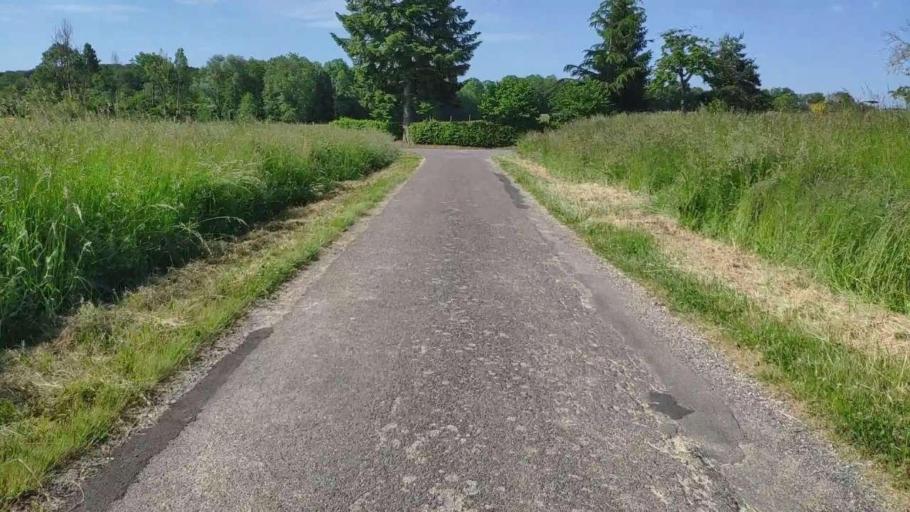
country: FR
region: Franche-Comte
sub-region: Departement du Jura
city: Bletterans
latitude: 46.7071
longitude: 5.4649
